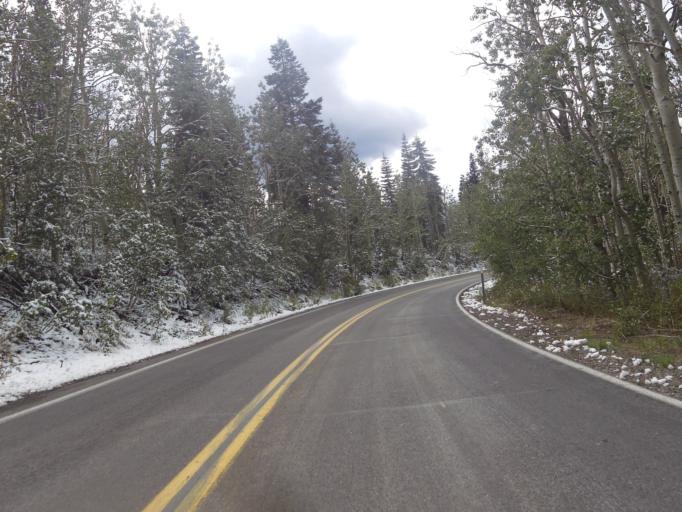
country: US
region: Nevada
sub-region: Douglas County
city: Gardnerville Ranchos
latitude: 38.6646
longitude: -119.6395
